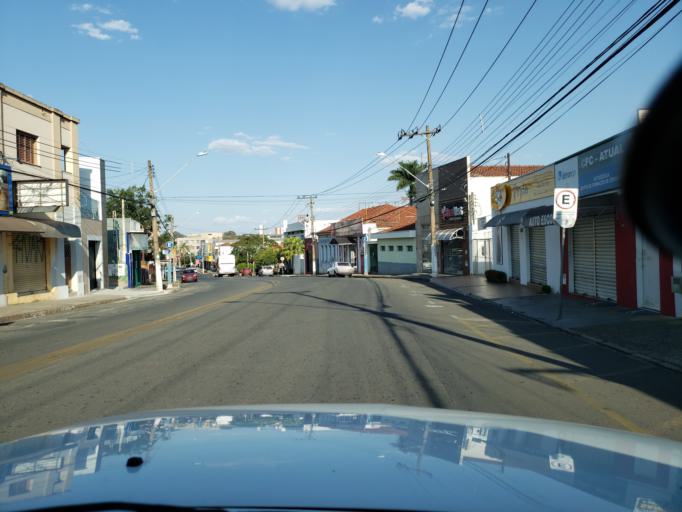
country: BR
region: Sao Paulo
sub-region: Moji-Guacu
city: Mogi-Gaucu
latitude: -22.3701
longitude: -46.9449
